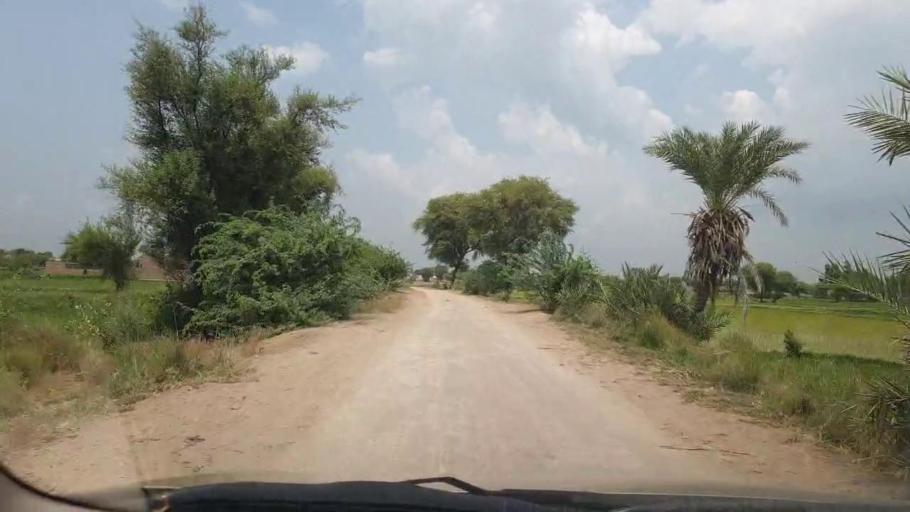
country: PK
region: Sindh
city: Larkana
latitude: 27.5724
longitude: 68.1238
